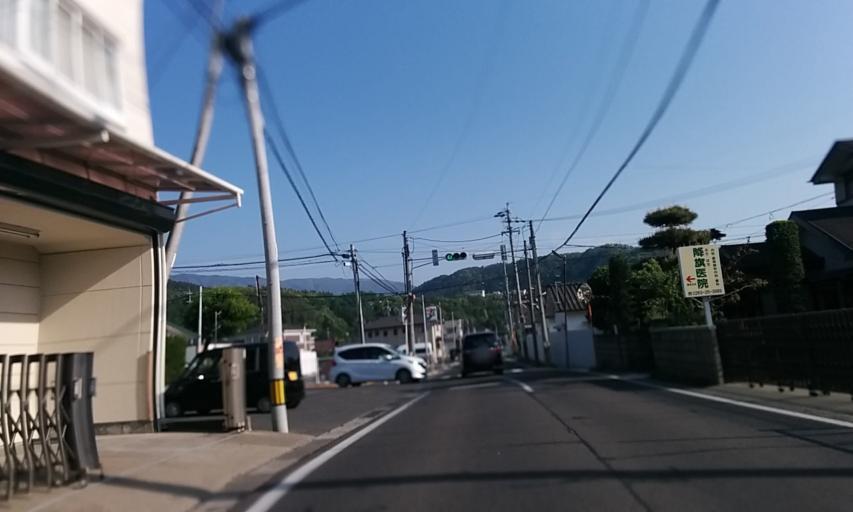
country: JP
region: Nagano
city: Matsumoto
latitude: 36.2212
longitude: 137.9864
